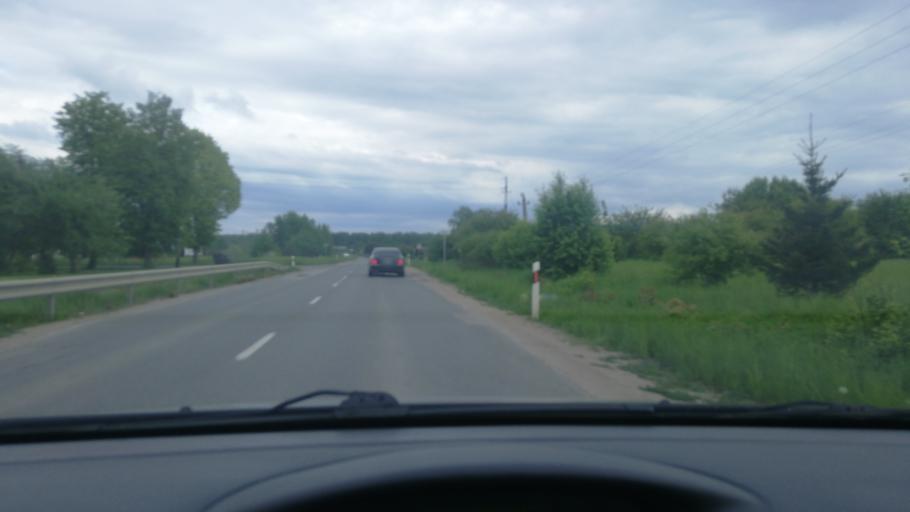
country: LT
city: Priekule
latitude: 55.6426
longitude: 21.2921
